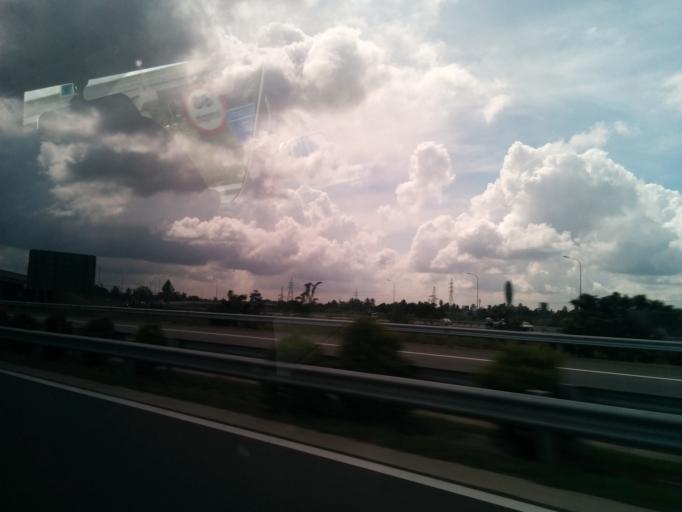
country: LK
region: Western
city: Peliyagoda
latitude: 6.9671
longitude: 79.8927
